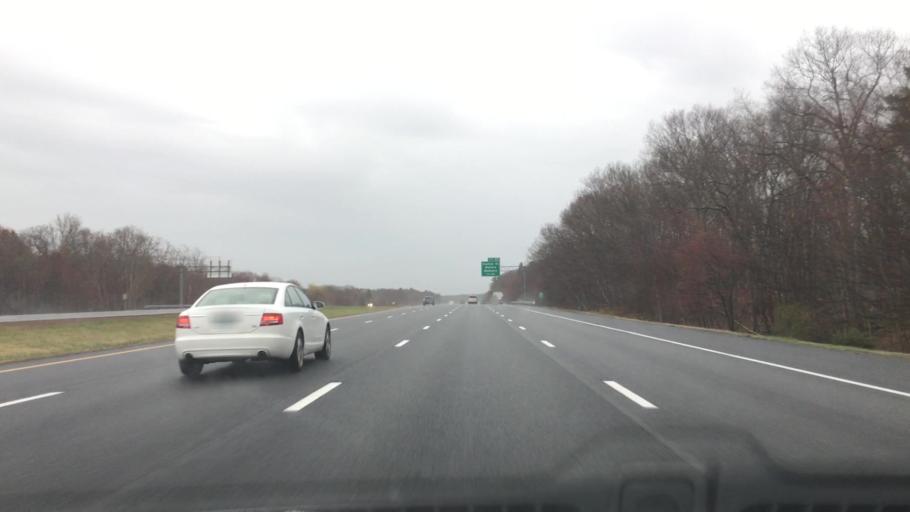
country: US
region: Massachusetts
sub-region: Essex County
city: West Newbury
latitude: 42.7662
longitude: -70.9358
